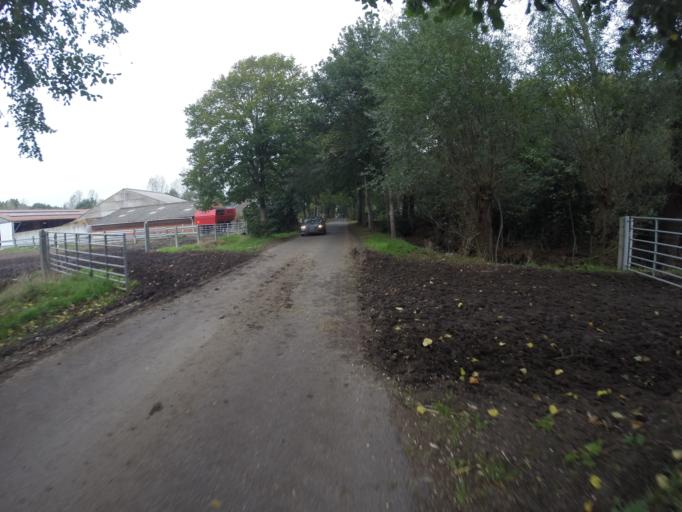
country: BE
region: Flanders
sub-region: Provincie West-Vlaanderen
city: Beernem
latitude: 51.1207
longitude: 3.3571
